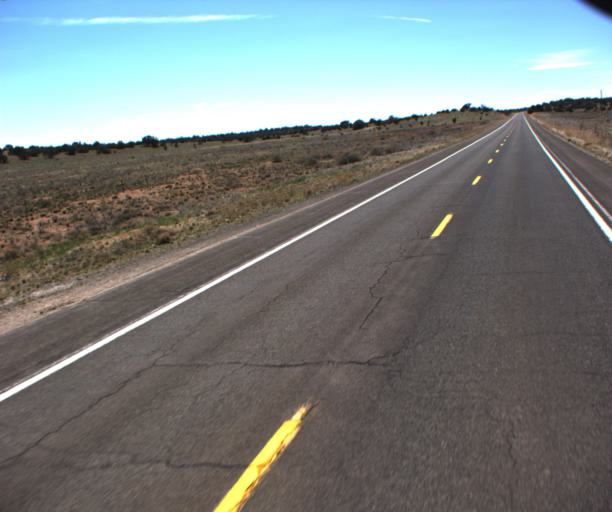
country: US
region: Arizona
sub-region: Mohave County
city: Peach Springs
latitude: 35.5530
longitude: -113.3408
